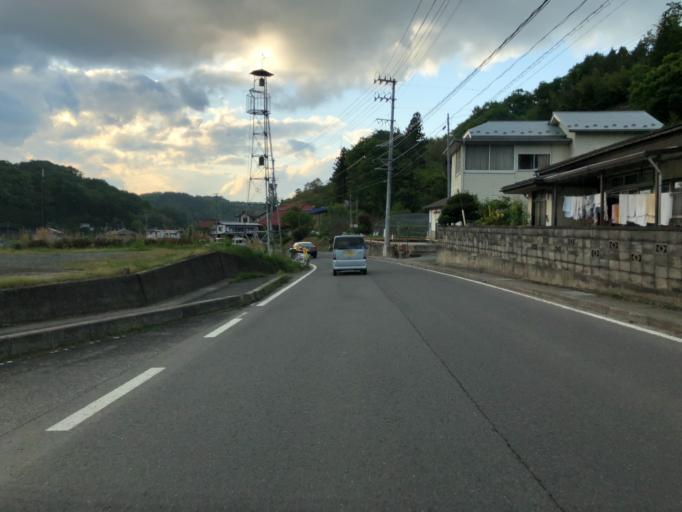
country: JP
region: Fukushima
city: Fukushima-shi
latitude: 37.6461
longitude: 140.6165
